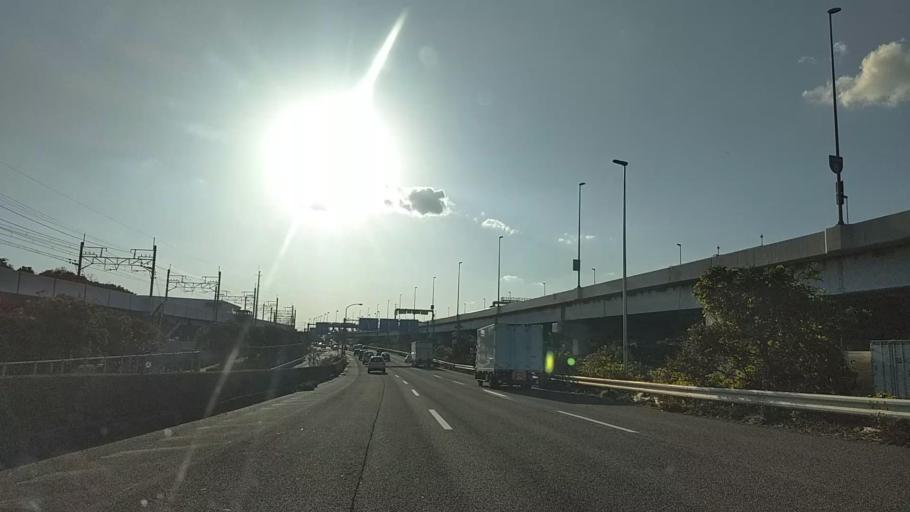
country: JP
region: Chiba
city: Funabashi
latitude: 35.6814
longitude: 139.9386
